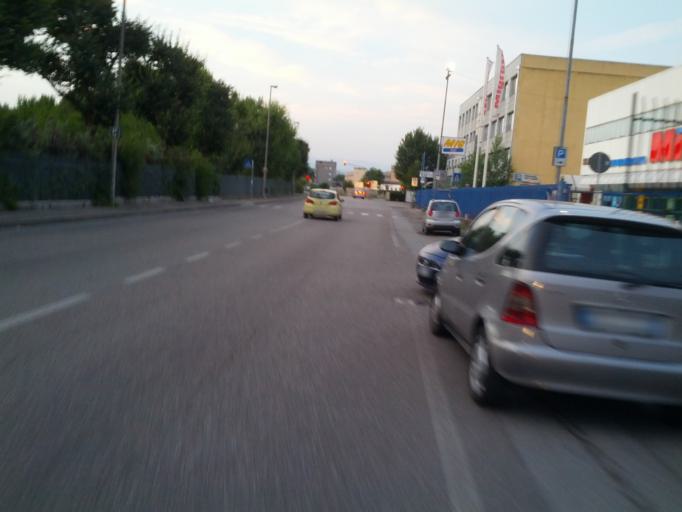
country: IT
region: Veneto
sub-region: Provincia di Verona
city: Verona
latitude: 45.4107
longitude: 10.9655
